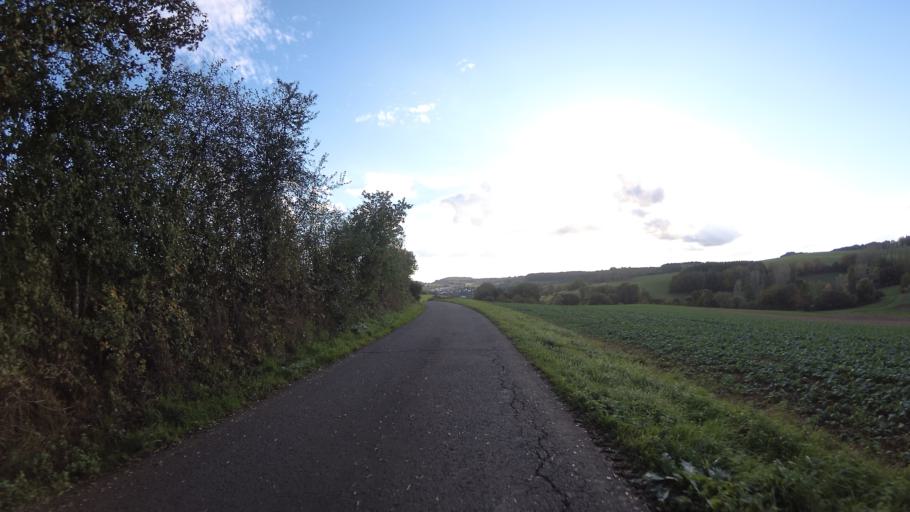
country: DE
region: Saarland
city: Marpingen
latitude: 49.4450
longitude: 7.0875
